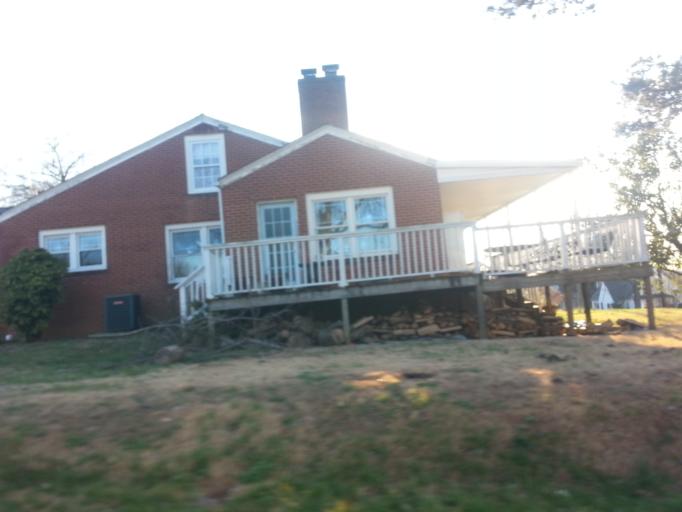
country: US
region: Tennessee
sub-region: Blount County
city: Maryville
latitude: 35.7660
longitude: -83.9582
